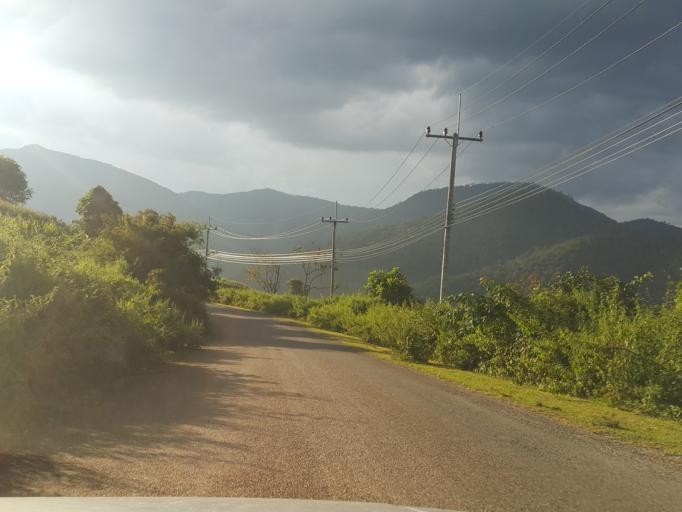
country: TH
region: Mae Hong Son
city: Khun Yuam
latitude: 18.7467
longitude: 98.2079
